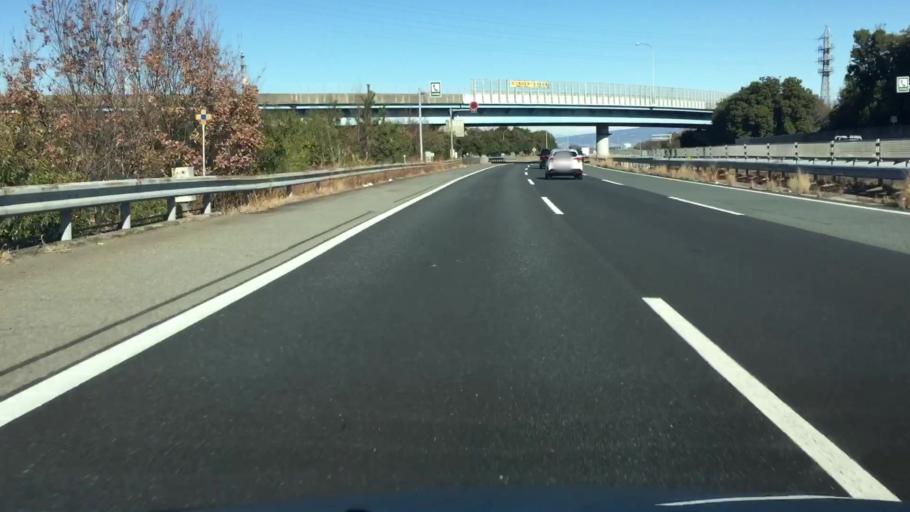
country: JP
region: Gunma
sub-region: Sawa-gun
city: Tamamura
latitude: 36.2727
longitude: 139.0955
